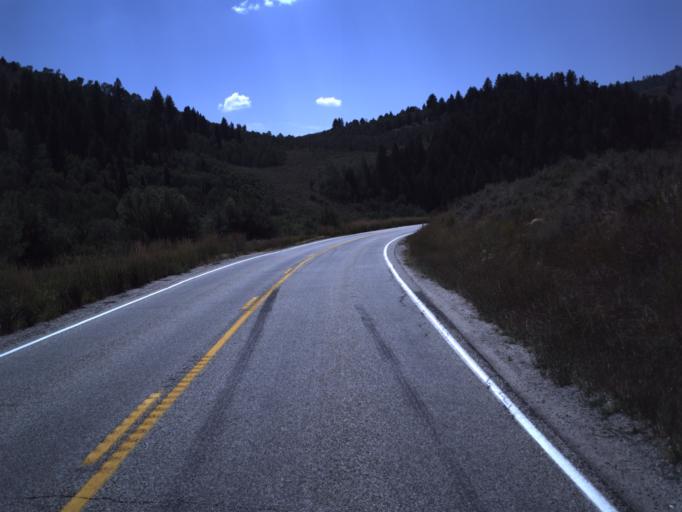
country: US
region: Utah
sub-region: Cache County
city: North Logan
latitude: 41.8586
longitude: -111.5763
